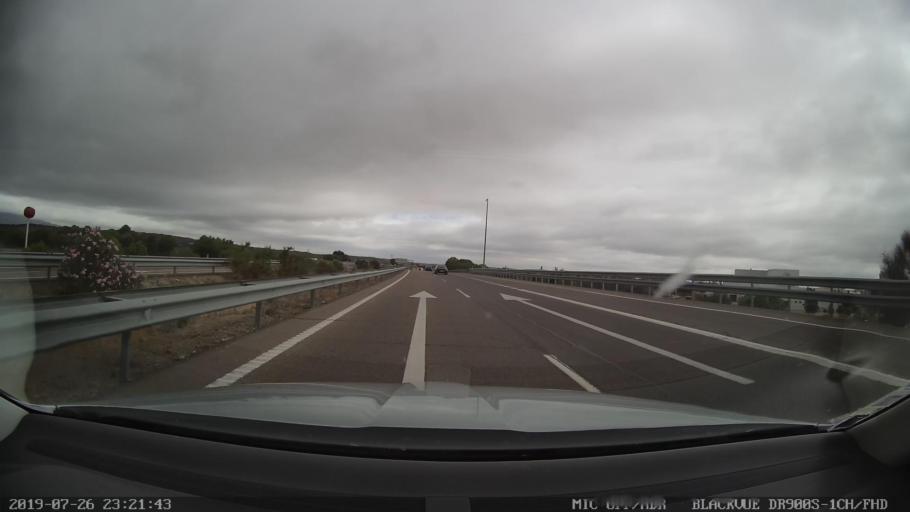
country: ES
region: Extremadura
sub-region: Provincia de Caceres
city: Miajadas
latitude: 39.1346
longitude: -5.9455
